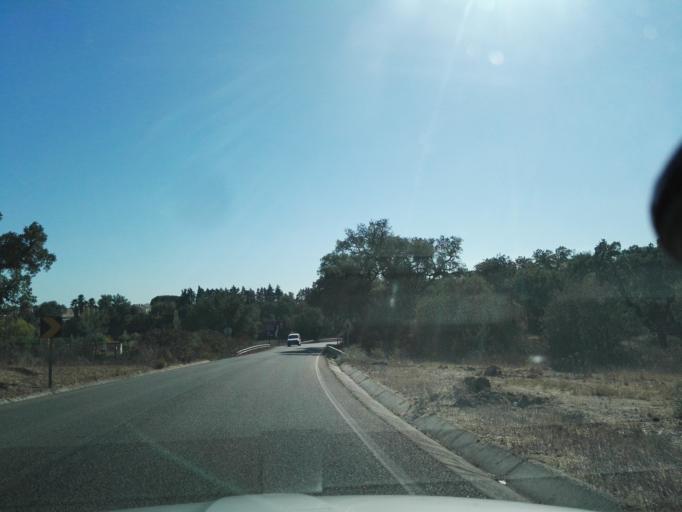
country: PT
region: Santarem
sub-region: Benavente
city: Poceirao
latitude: 38.8697
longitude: -8.7470
